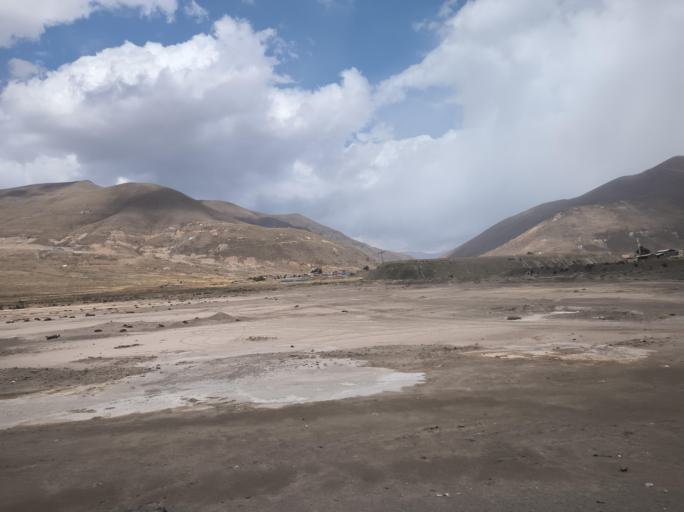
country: BO
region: Oruro
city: Poopo
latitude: -18.3788
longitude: -66.9797
